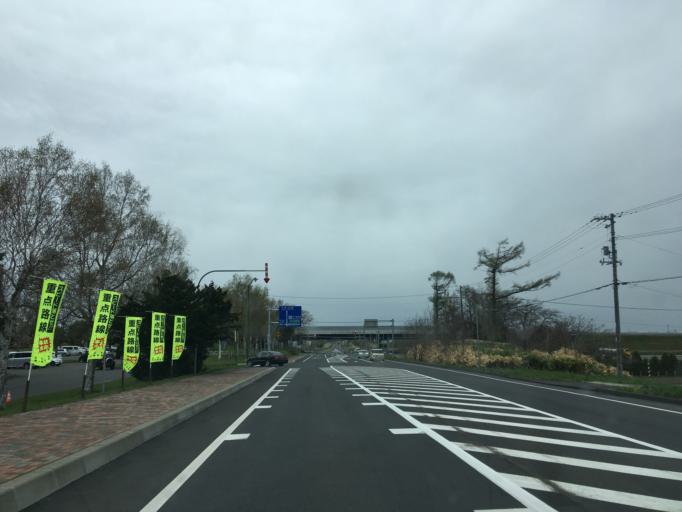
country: JP
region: Hokkaido
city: Chitose
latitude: 42.9501
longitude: 141.7173
